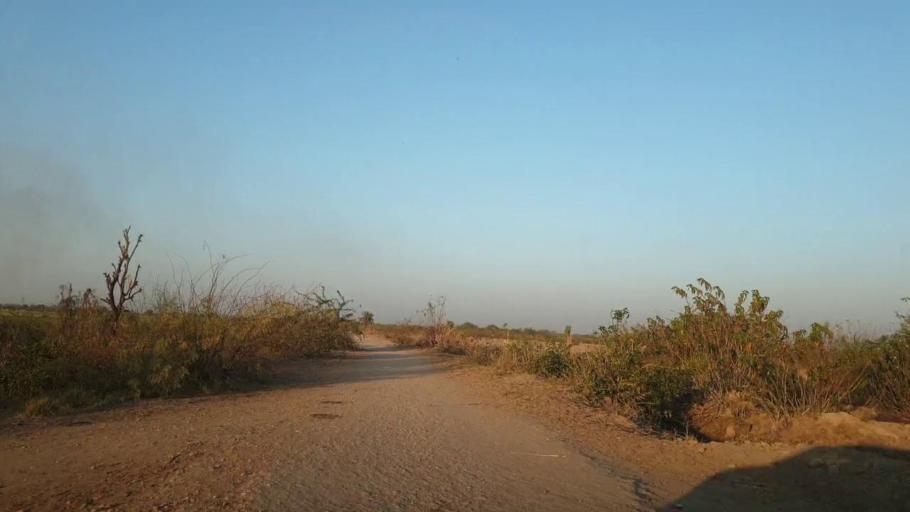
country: PK
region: Sindh
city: Mirpur Khas
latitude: 25.7180
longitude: 69.0642
